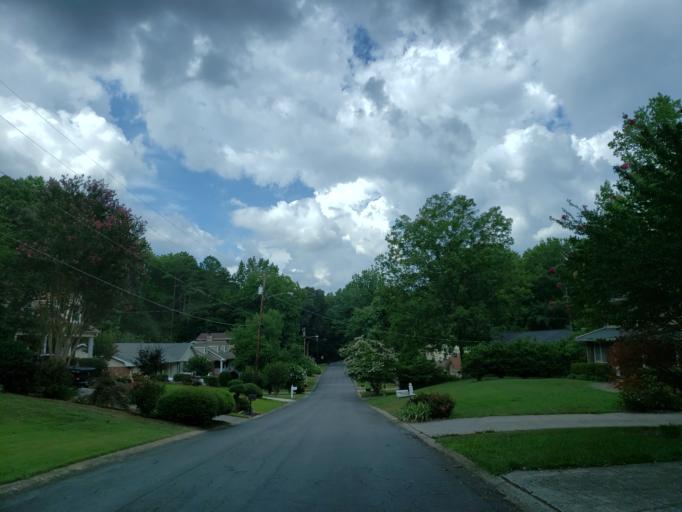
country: US
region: Georgia
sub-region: Fulton County
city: Sandy Springs
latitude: 33.9778
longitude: -84.4318
